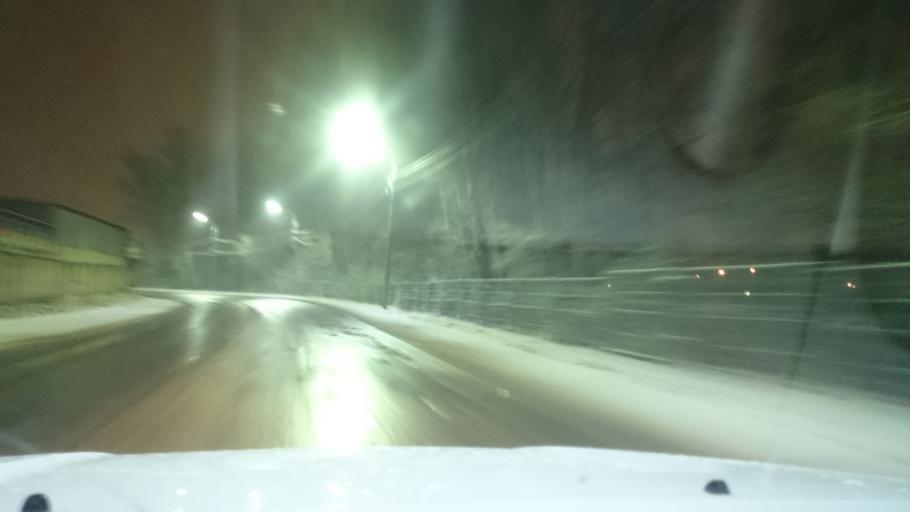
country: RU
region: Tula
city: Gorelki
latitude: 54.2232
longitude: 37.5846
